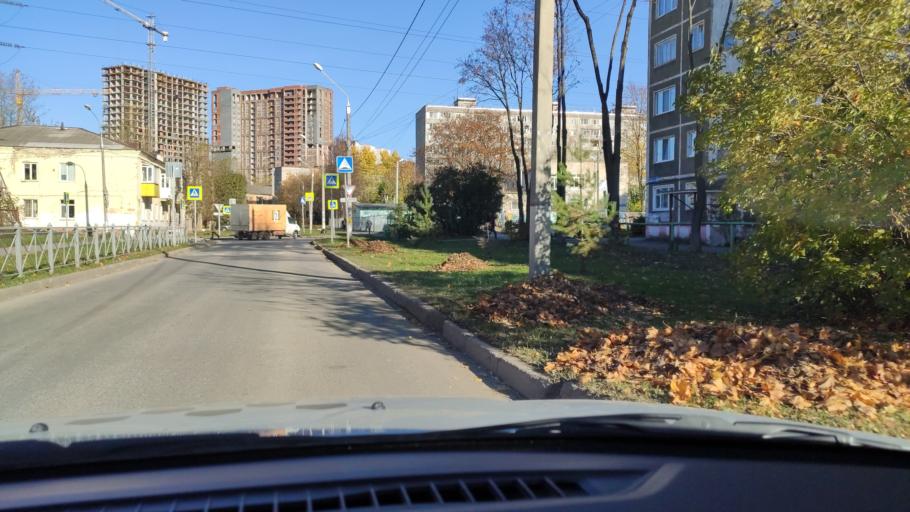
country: RU
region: Perm
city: Perm
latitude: 57.9816
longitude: 56.2102
